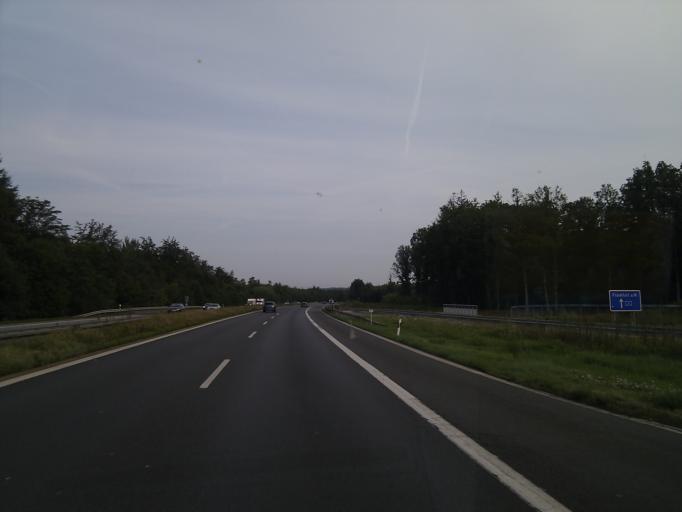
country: DE
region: Bavaria
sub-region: Regierungsbezirk Unterfranken
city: Esselbach
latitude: 49.8379
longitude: 9.5134
